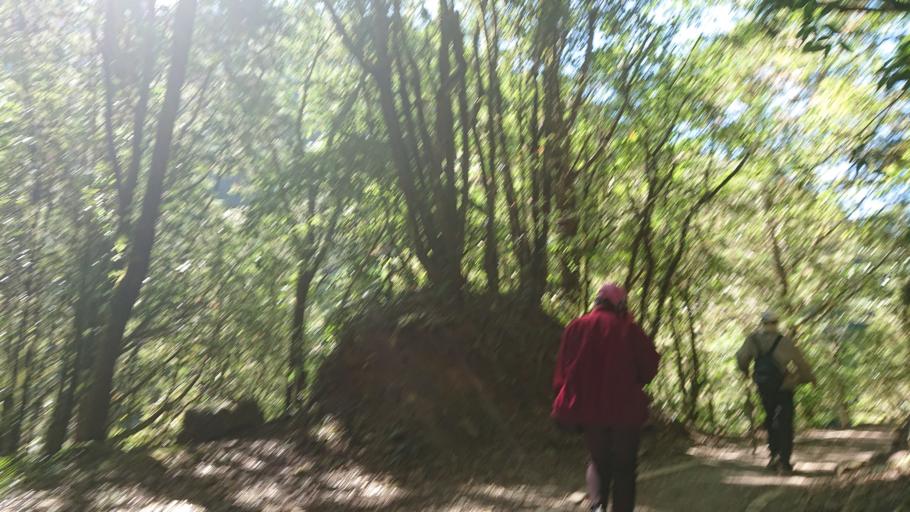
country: TW
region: Taiwan
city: Lugu
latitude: 23.4792
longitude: 120.8261
